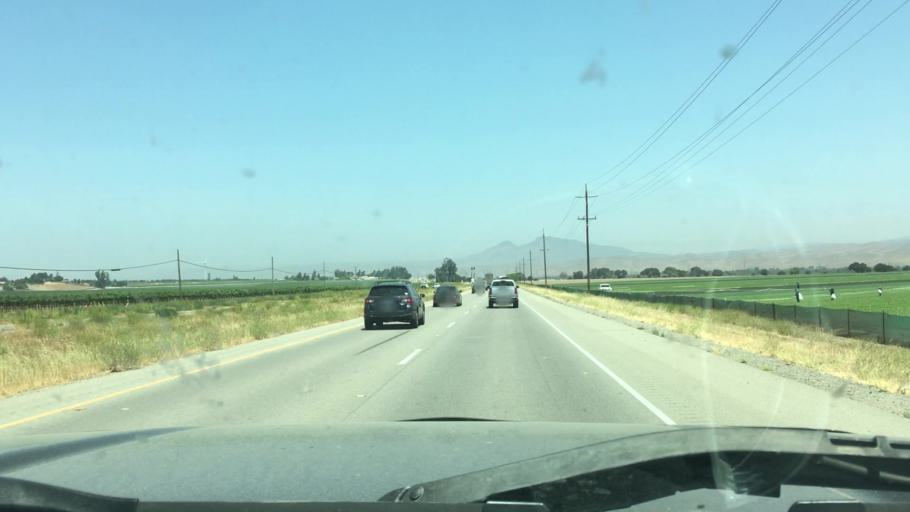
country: US
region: California
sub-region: Monterey County
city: King City
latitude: 36.2447
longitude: -121.1771
